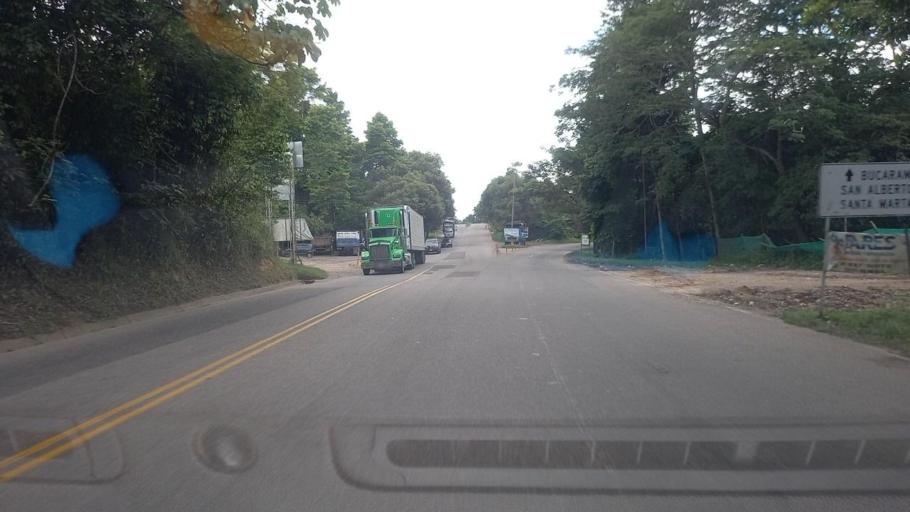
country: CO
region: Santander
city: Sabana de Torres
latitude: 7.1300
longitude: -73.5648
